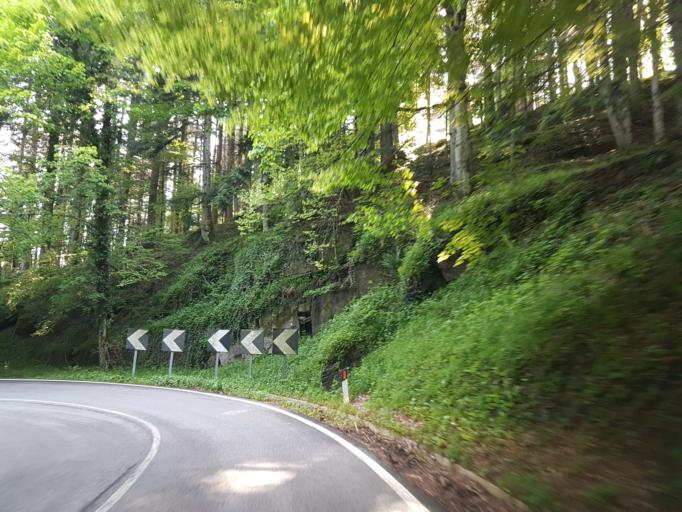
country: IT
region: Tuscany
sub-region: Province of Arezzo
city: Soci
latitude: 43.7966
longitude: 11.8882
